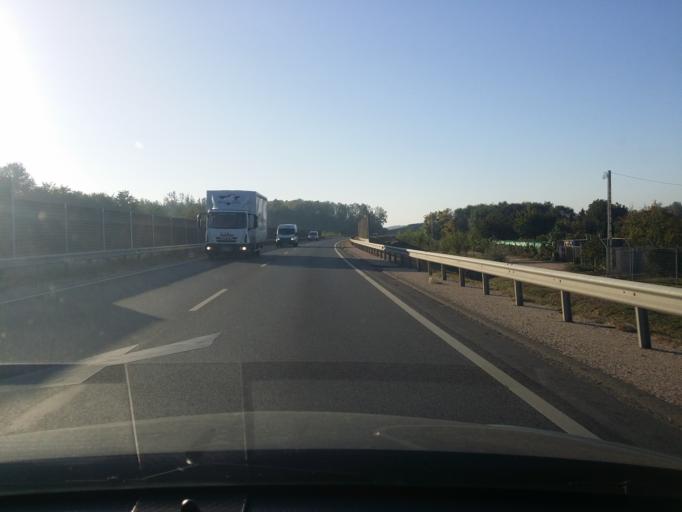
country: HU
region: Bacs-Kiskun
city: Kecskemet
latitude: 46.9386
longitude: 19.7111
